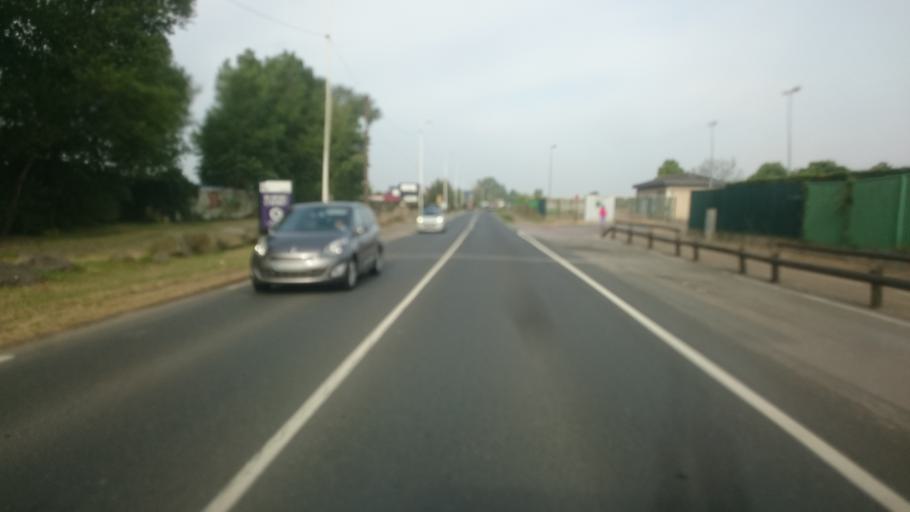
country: FR
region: Pays de la Loire
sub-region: Departement de la Loire-Atlantique
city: Bouguenais
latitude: 47.1946
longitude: -1.6216
